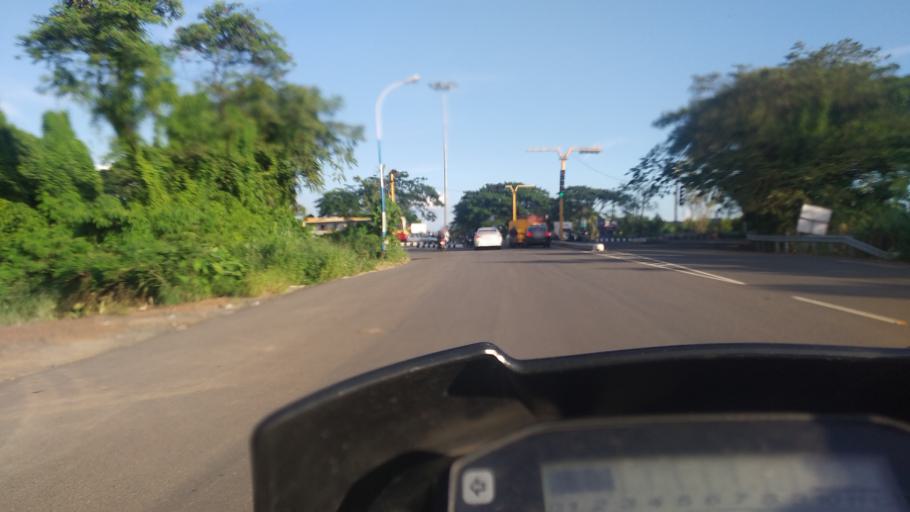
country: IN
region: Kerala
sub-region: Ernakulam
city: Cochin
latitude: 9.9361
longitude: 76.2711
